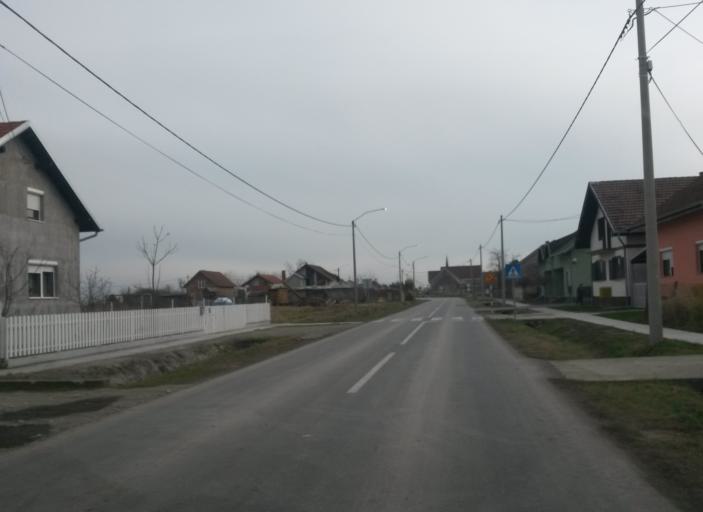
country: HR
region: Osjecko-Baranjska
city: Antunovac
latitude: 45.4891
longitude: 18.6301
